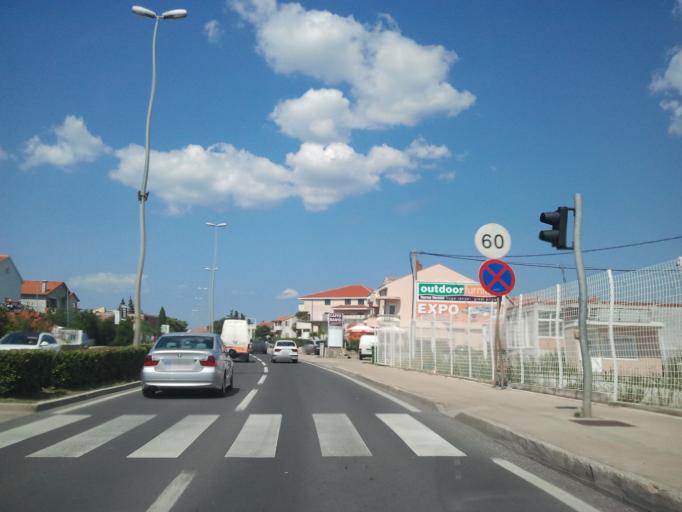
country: HR
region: Zadarska
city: Zadar
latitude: 44.1095
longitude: 15.2596
